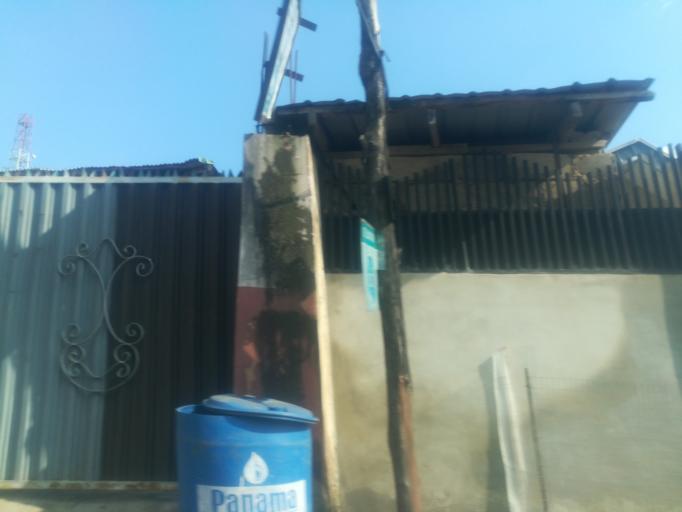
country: NG
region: Oyo
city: Ibadan
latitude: 7.4222
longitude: 3.8410
